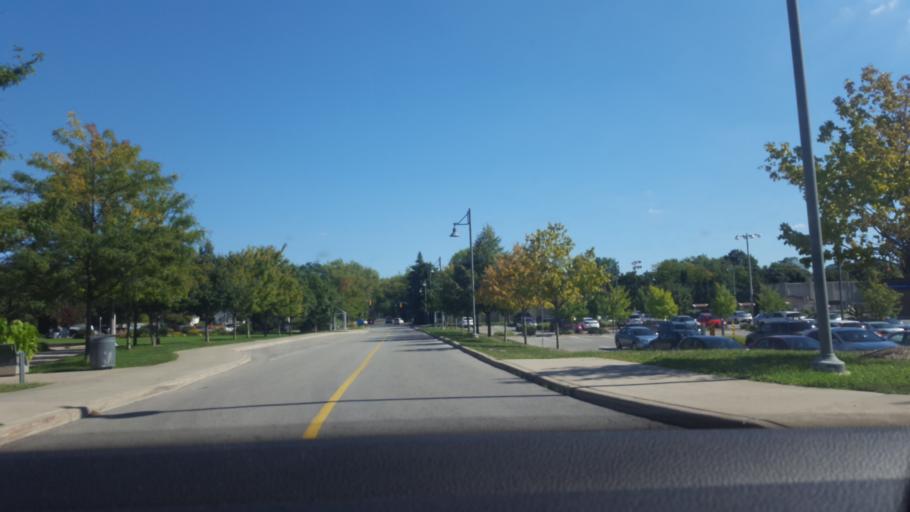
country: CA
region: Ontario
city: Burlington
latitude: 43.3355
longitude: -79.7914
